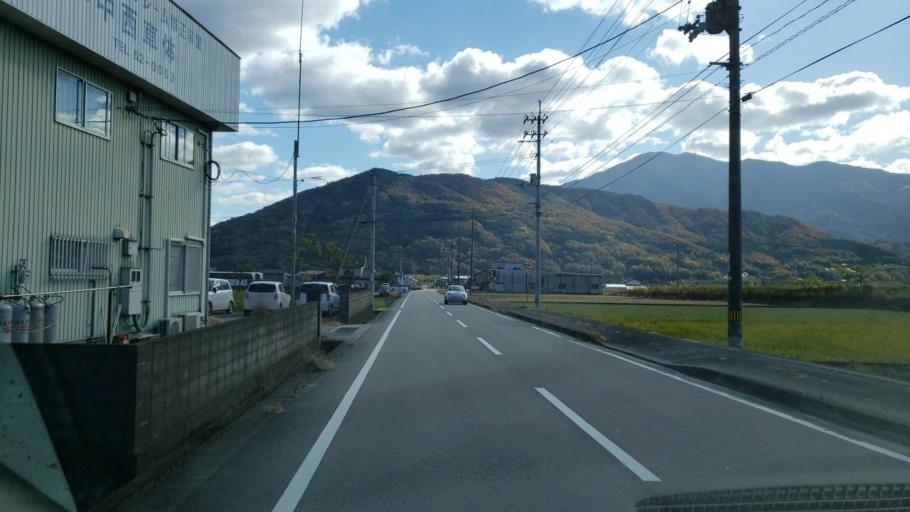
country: JP
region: Tokushima
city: Wakimachi
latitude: 34.0717
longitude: 134.1787
